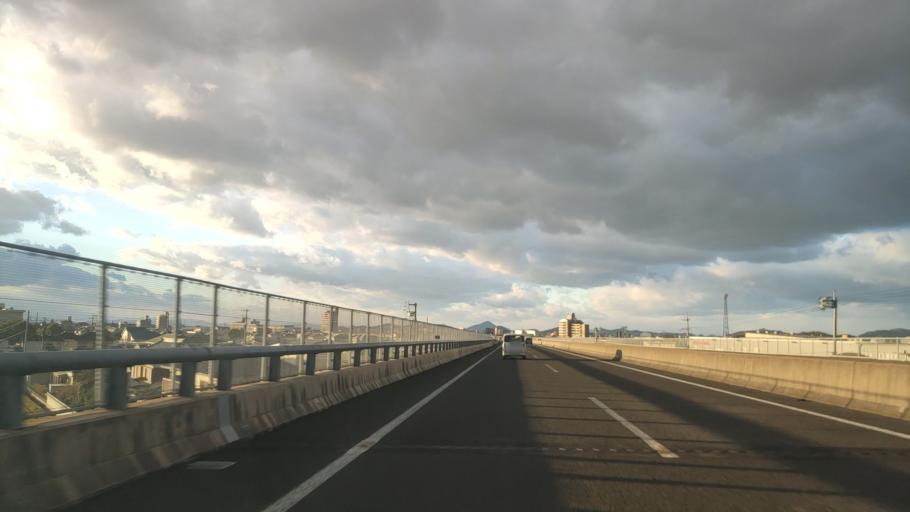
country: JP
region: Ehime
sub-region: Shikoku-chuo Shi
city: Matsuyama
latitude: 33.7927
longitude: 132.8015
